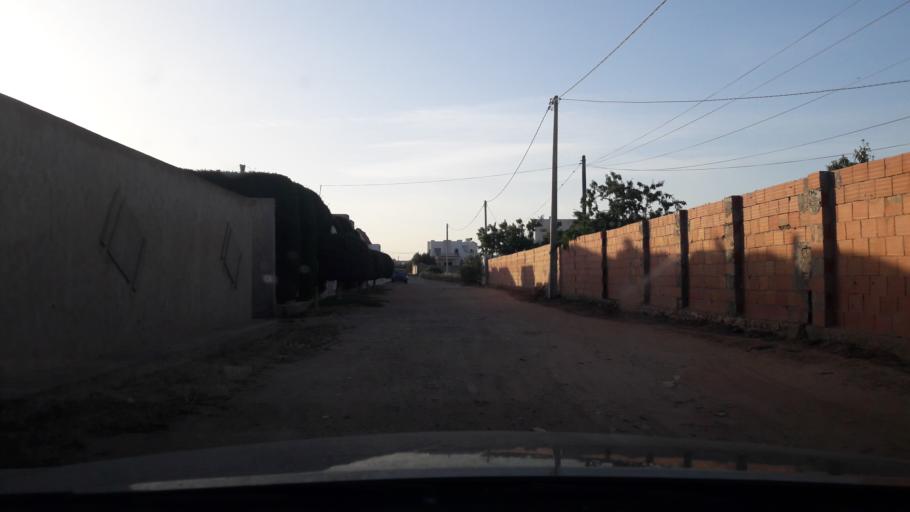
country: TN
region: Safaqis
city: Al Qarmadah
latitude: 34.7931
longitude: 10.7530
